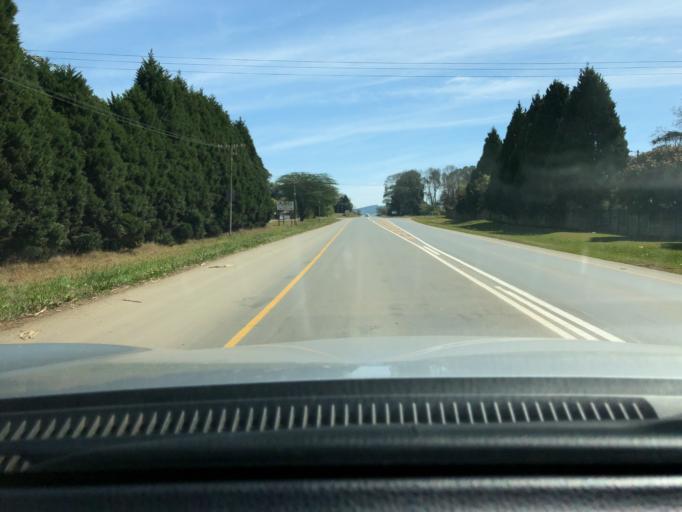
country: ZA
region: KwaZulu-Natal
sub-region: uMgungundlovu District Municipality
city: Richmond
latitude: -29.8848
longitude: 30.2875
